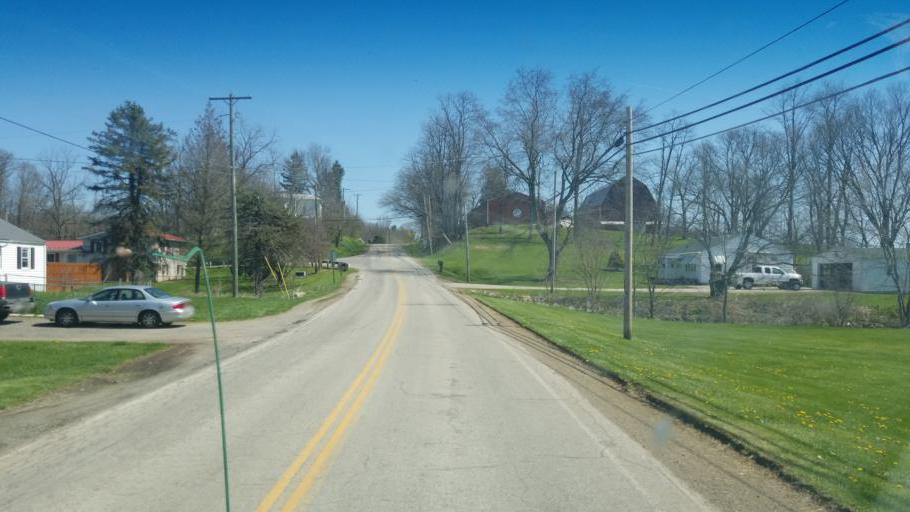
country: US
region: Ohio
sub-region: Richland County
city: Lincoln Heights
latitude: 40.8095
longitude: -82.4349
